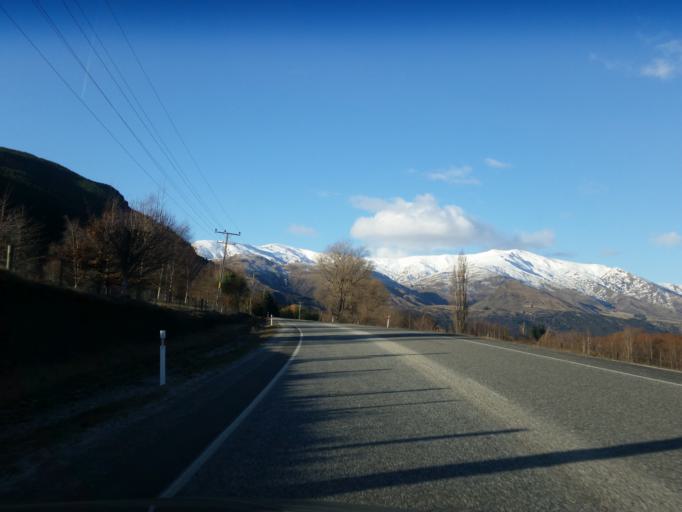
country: NZ
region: Otago
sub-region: Queenstown-Lakes District
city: Arrowtown
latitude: -44.9467
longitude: 168.7845
